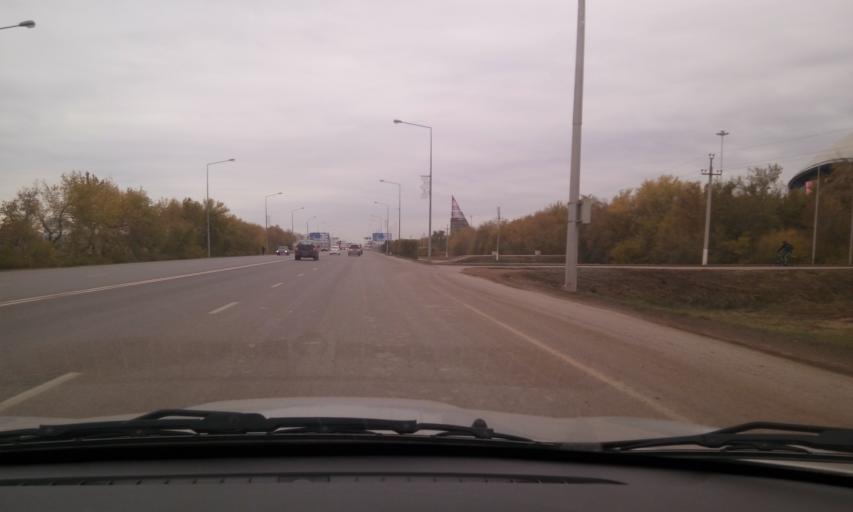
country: KZ
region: Astana Qalasy
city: Astana
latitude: 51.1110
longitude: 71.4102
